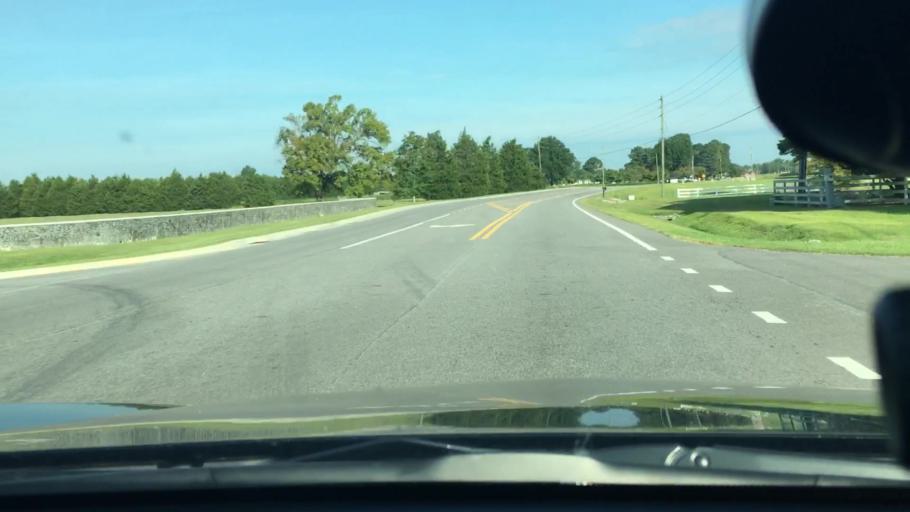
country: US
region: North Carolina
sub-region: Pitt County
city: Summerfield
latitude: 35.6457
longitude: -77.4595
